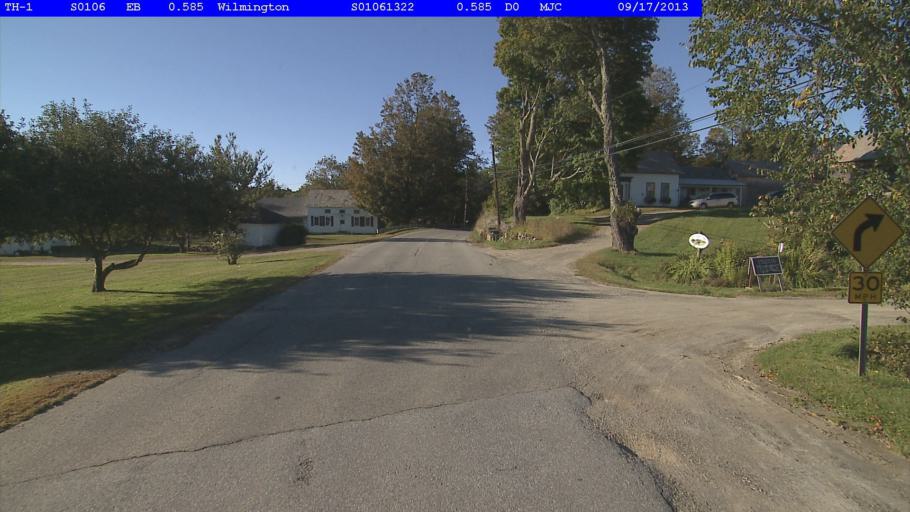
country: US
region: Vermont
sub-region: Windham County
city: Dover
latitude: 42.9205
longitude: -72.8362
